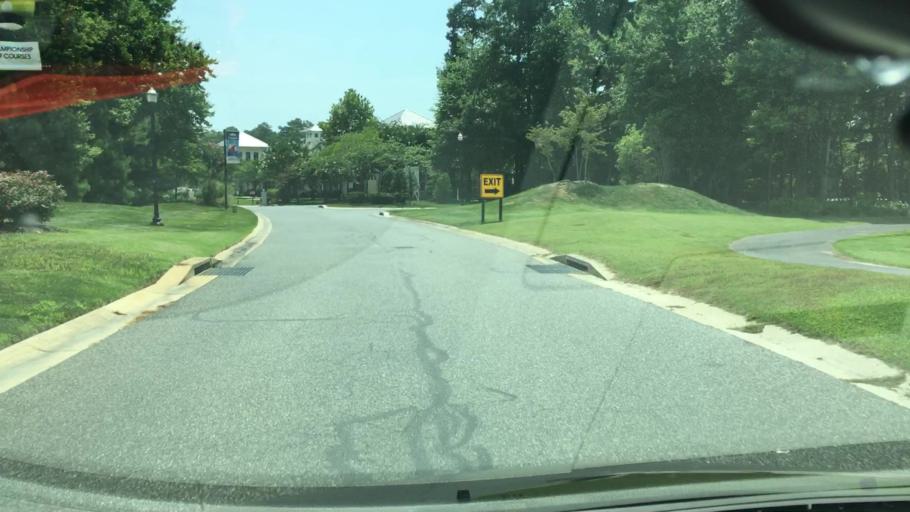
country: US
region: Maryland
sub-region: Worcester County
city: West Ocean City
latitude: 38.3427
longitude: -75.1539
